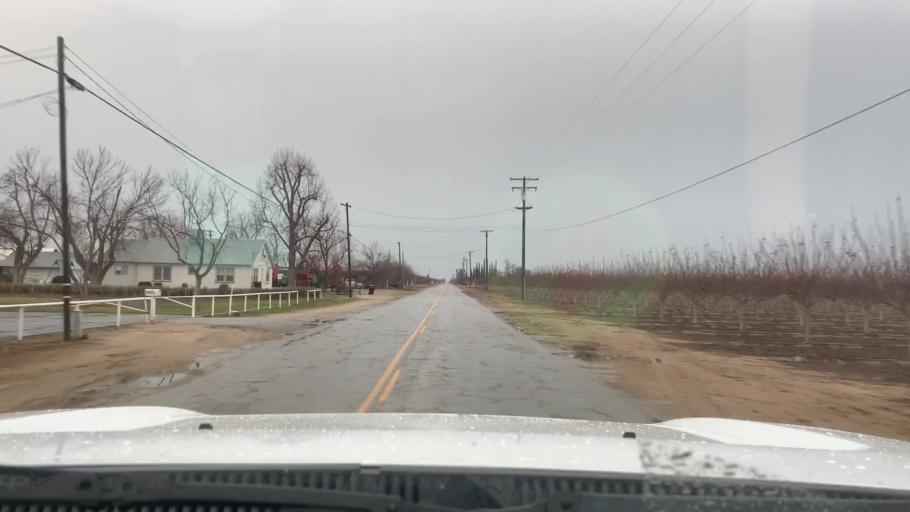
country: US
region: California
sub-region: Kern County
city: Shafter
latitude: 35.4781
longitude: -119.2833
